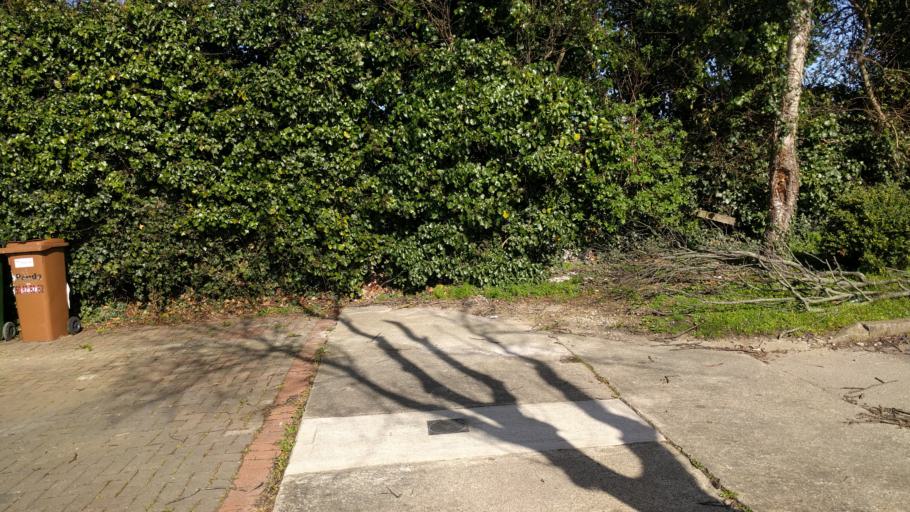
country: IE
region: Leinster
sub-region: Fingal County
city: Swords
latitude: 53.4570
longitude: -6.2163
